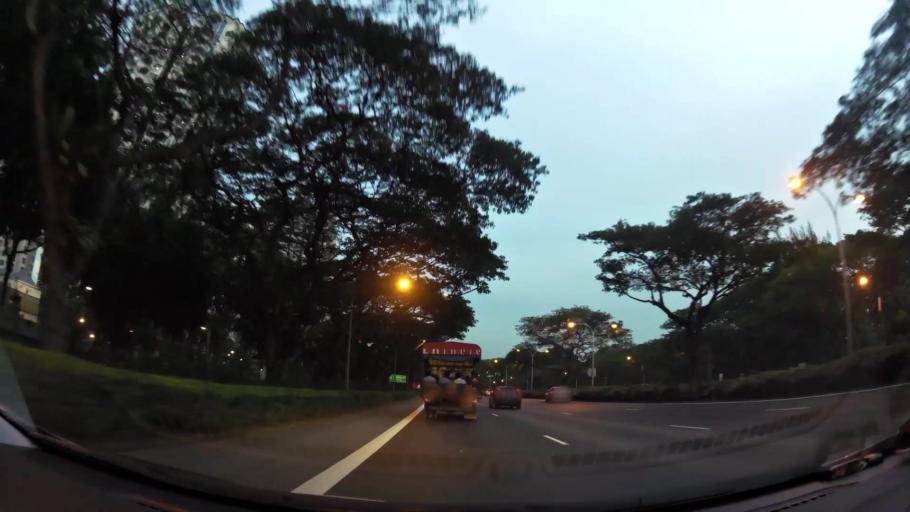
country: SG
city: Singapore
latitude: 1.2962
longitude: 103.8947
